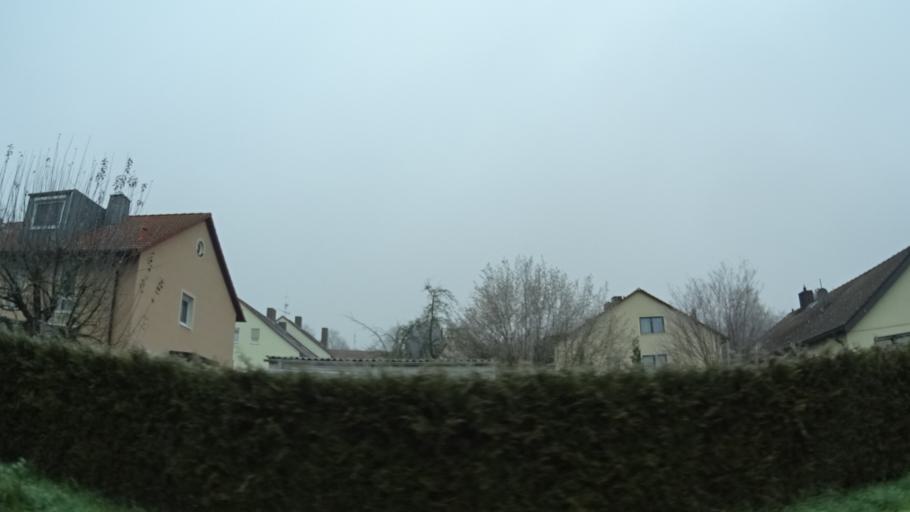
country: DE
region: Bavaria
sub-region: Regierungsbezirk Unterfranken
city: Kitzingen
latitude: 49.7249
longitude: 10.1537
